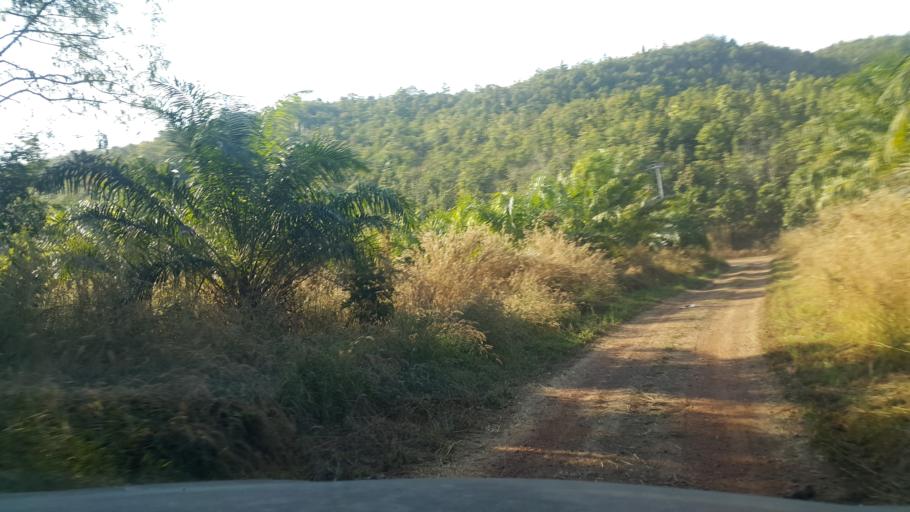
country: TH
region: Lamphun
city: Mae Tha
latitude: 18.5270
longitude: 99.1235
